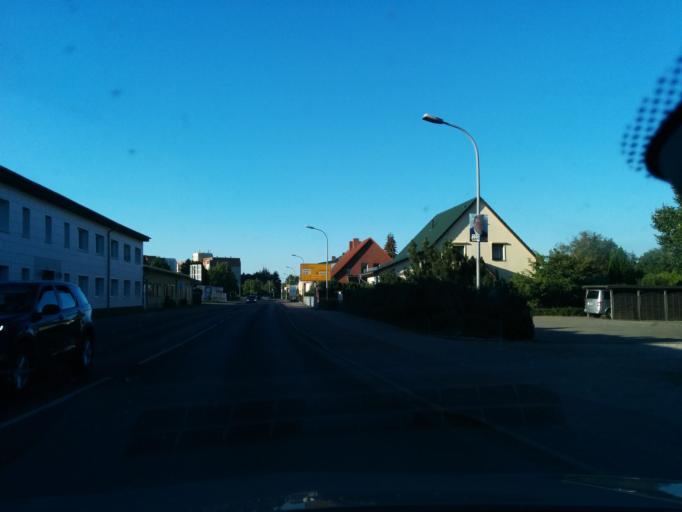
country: DE
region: Mecklenburg-Vorpommern
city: Ueckermunde
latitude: 53.7315
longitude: 14.0353
